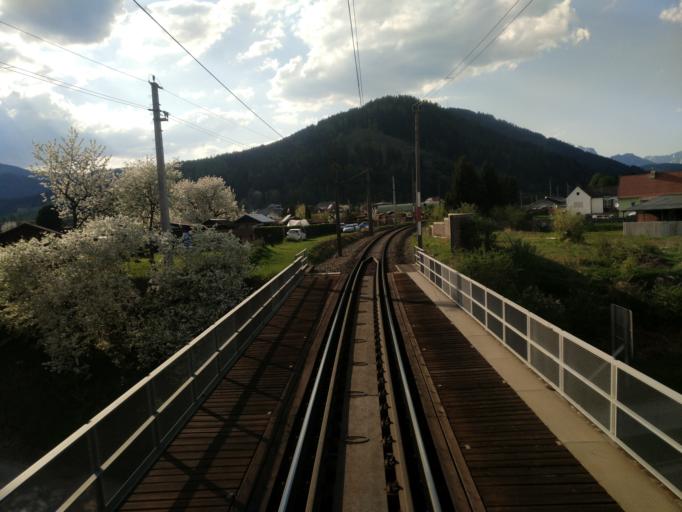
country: AT
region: Styria
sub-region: Politischer Bezirk Leoben
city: Sankt Michael in Obersteiermark
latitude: 47.3404
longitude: 15.0137
